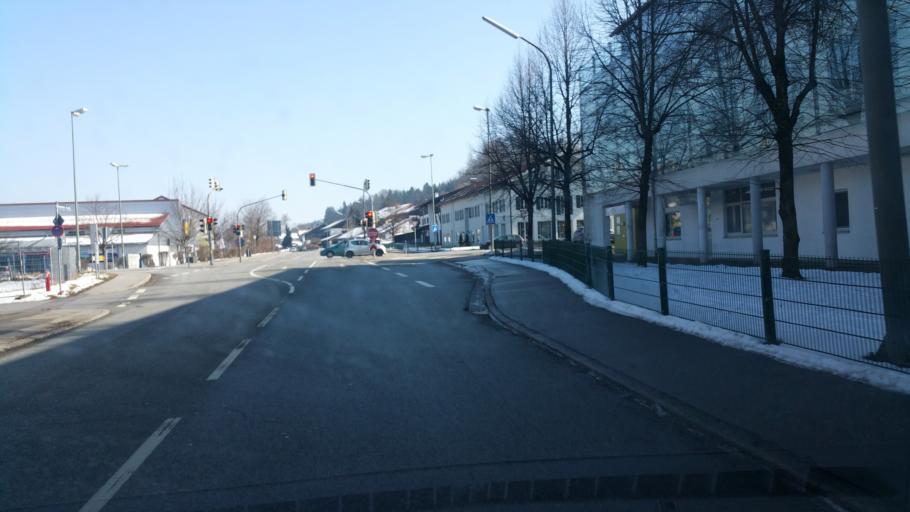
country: DE
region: Bavaria
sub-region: Upper Bavaria
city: Miesbach
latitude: 47.7890
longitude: 11.8381
